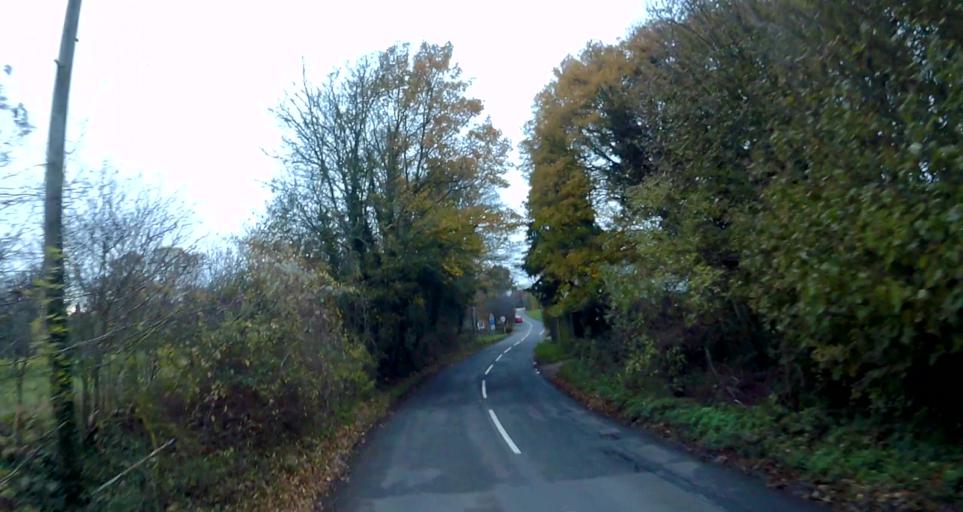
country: GB
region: England
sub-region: Hampshire
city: Odiham
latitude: 51.2496
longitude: -0.9368
